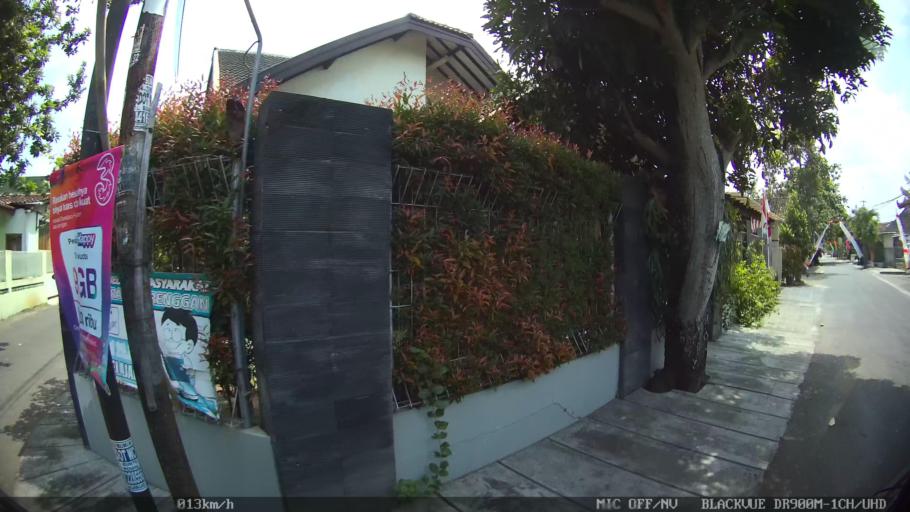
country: ID
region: Daerah Istimewa Yogyakarta
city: Yogyakarta
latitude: -7.8172
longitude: 110.3968
